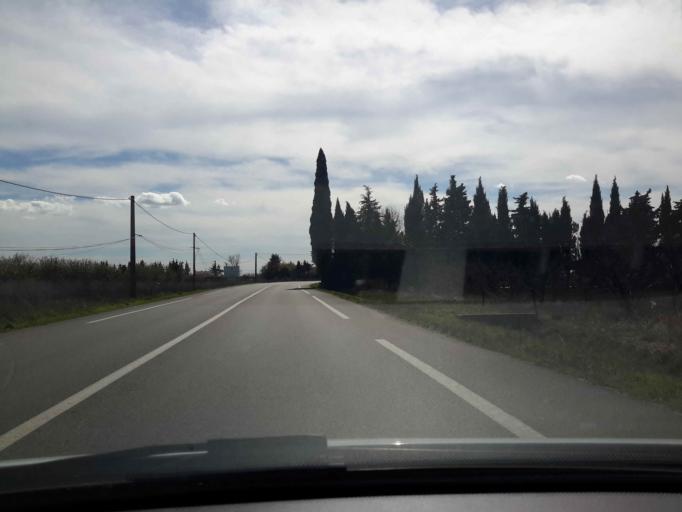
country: FR
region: Languedoc-Roussillon
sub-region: Departement du Gard
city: Vauvert
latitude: 43.6985
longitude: 4.2540
